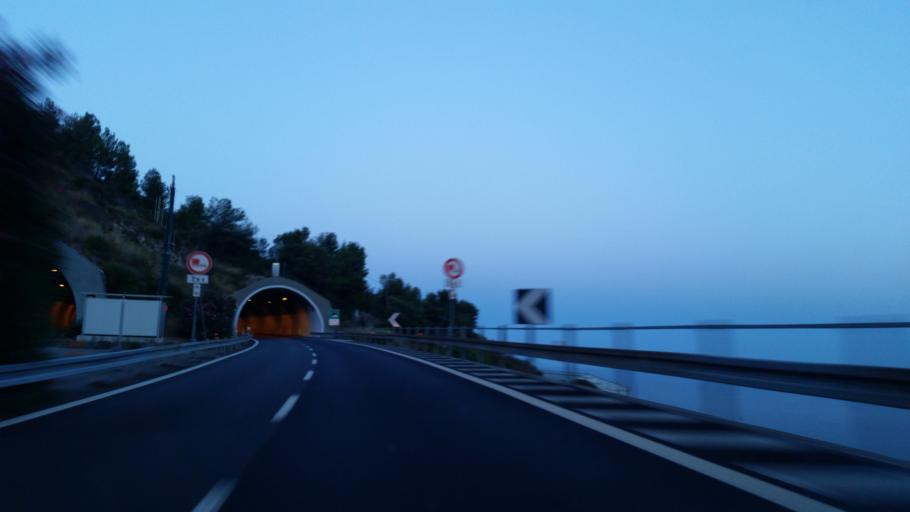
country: IT
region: Liguria
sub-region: Provincia di Imperia
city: Bordighera
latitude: 43.7932
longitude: 7.6813
